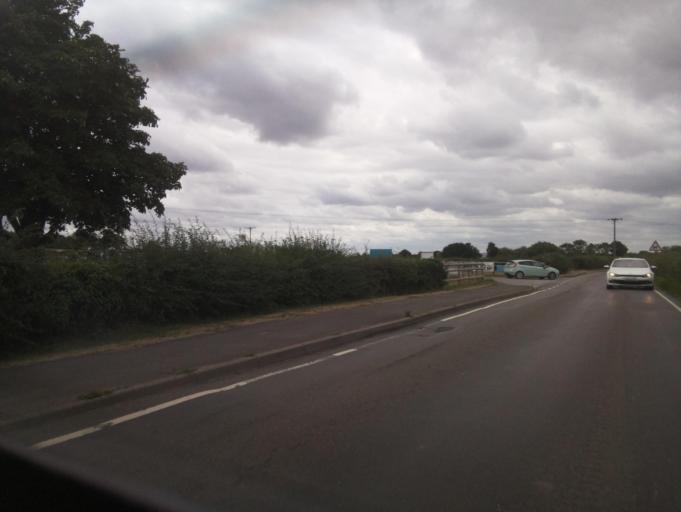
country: GB
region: England
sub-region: Derbyshire
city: Long Eaton
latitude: 52.9083
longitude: -1.3188
